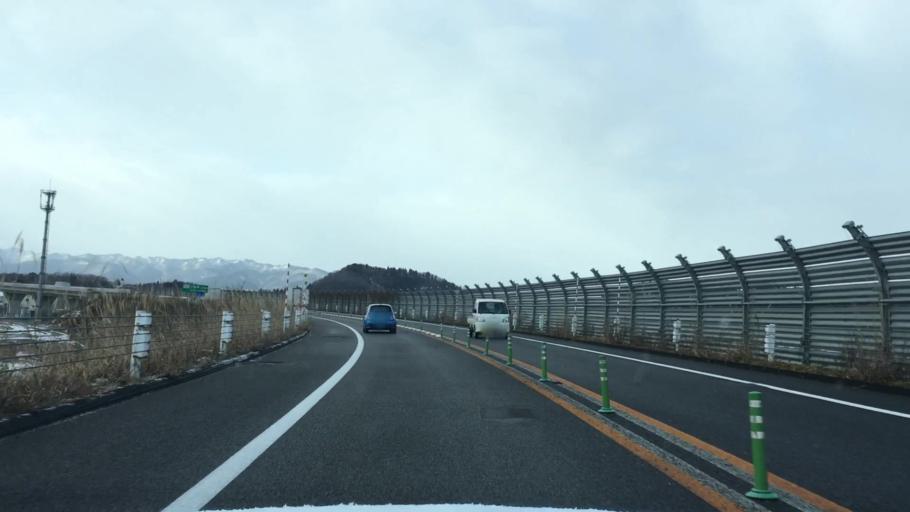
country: JP
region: Akita
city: Odate
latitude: 40.2885
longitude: 140.5430
